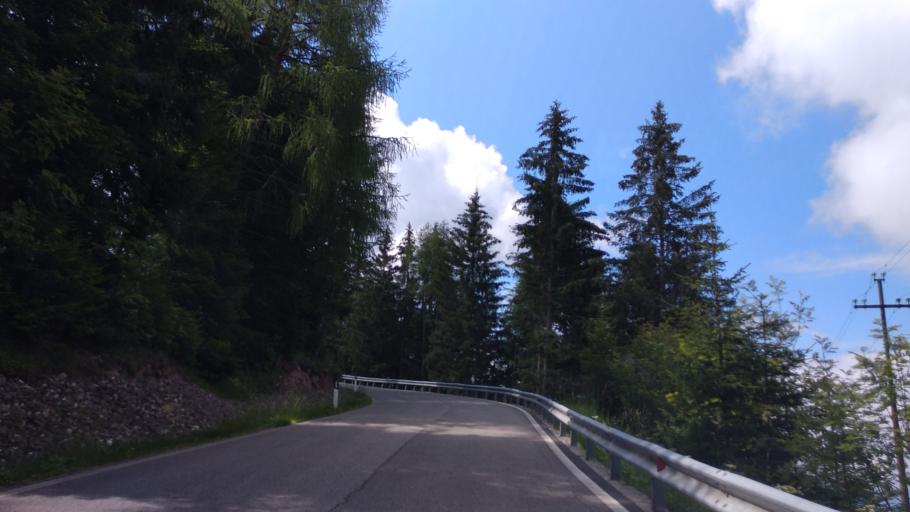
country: IT
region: Trentino-Alto Adige
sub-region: Bolzano
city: Avelengo
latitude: 46.6571
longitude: 11.2287
